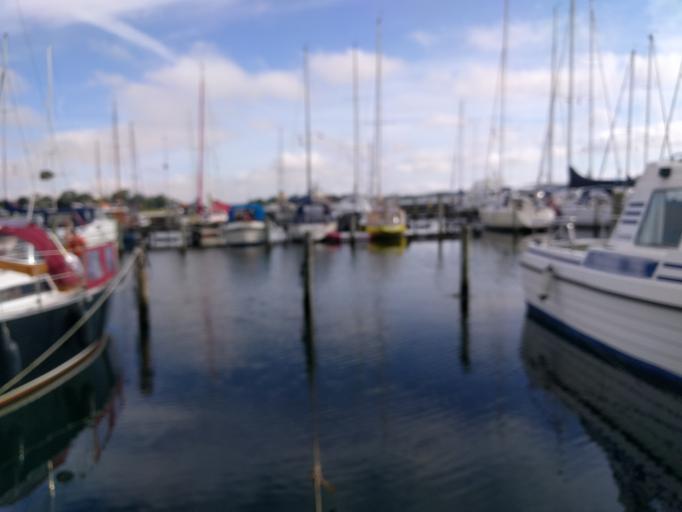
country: DK
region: South Denmark
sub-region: Kerteminde Kommune
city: Kerteminde
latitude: 55.4544
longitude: 10.6666
